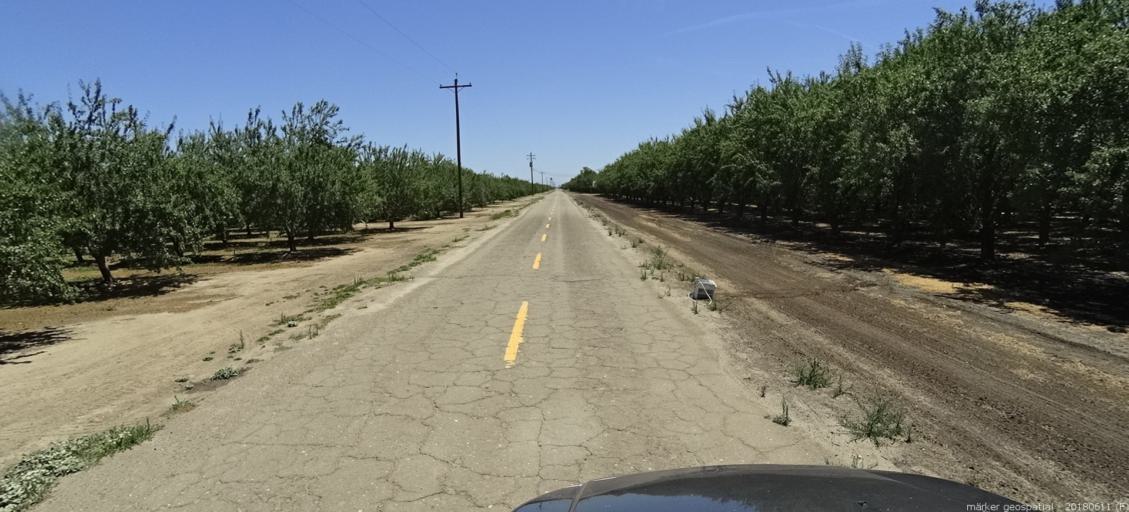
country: US
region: California
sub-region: Madera County
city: Fairmead
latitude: 37.0546
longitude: -120.2084
